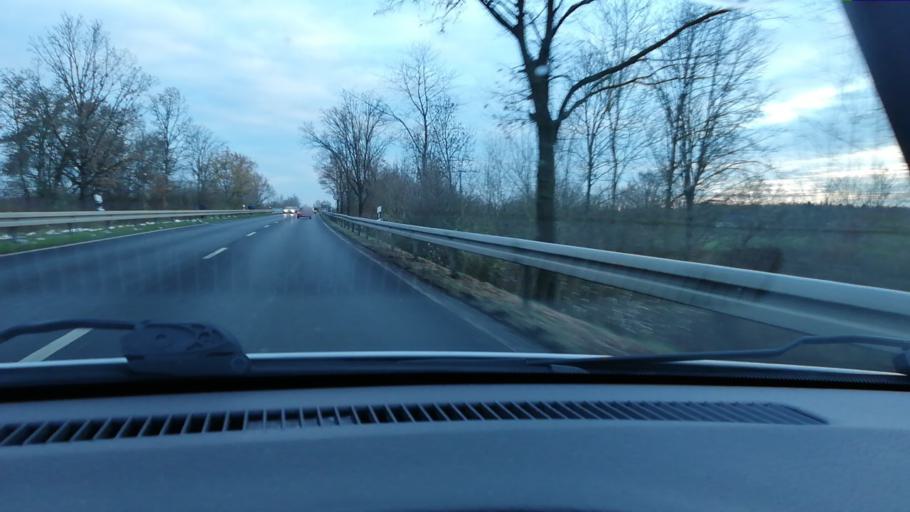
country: DE
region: Hesse
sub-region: Regierungsbezirk Darmstadt
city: Erlensee
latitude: 50.1505
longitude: 8.9997
